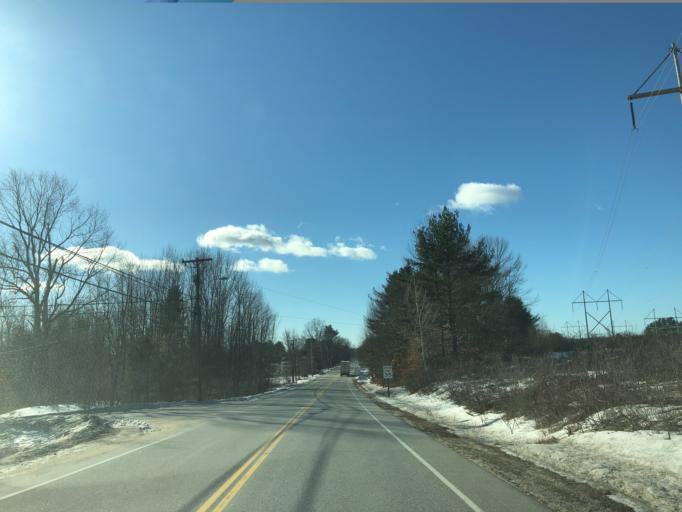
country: US
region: Maine
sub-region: Cumberland County
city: South Windham
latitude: 43.7515
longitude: -70.4247
